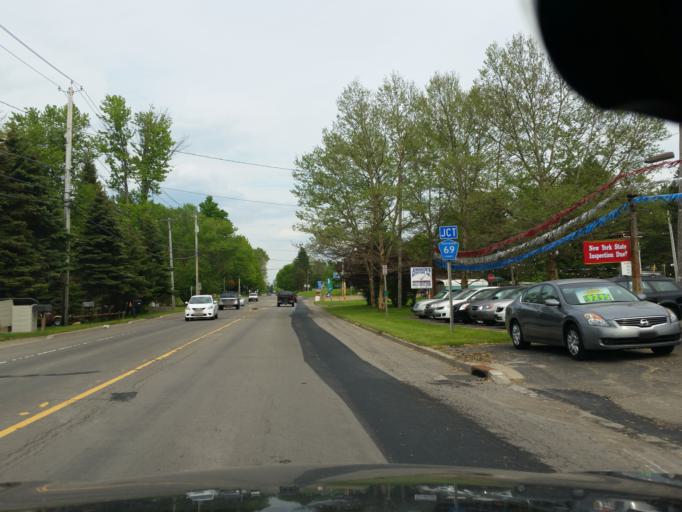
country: US
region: New York
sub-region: Chautauqua County
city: Lakewood
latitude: 42.0990
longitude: -79.3502
